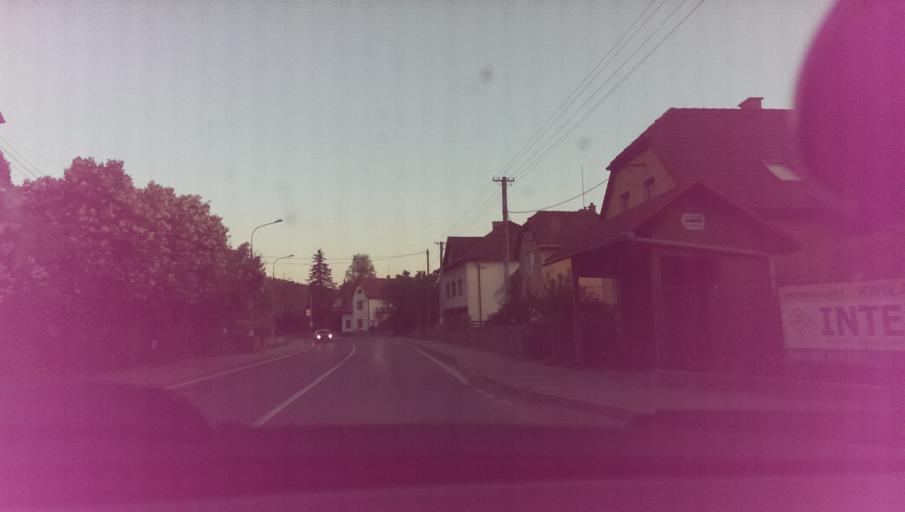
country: CZ
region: Zlin
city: Jablunka
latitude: 49.3877
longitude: 17.9494
